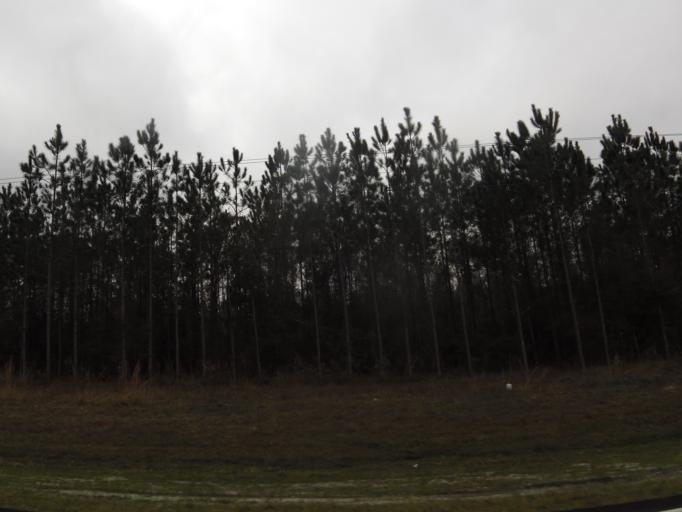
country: US
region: Florida
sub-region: Gilchrist County
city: Trenton
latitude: 29.7903
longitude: -82.7949
